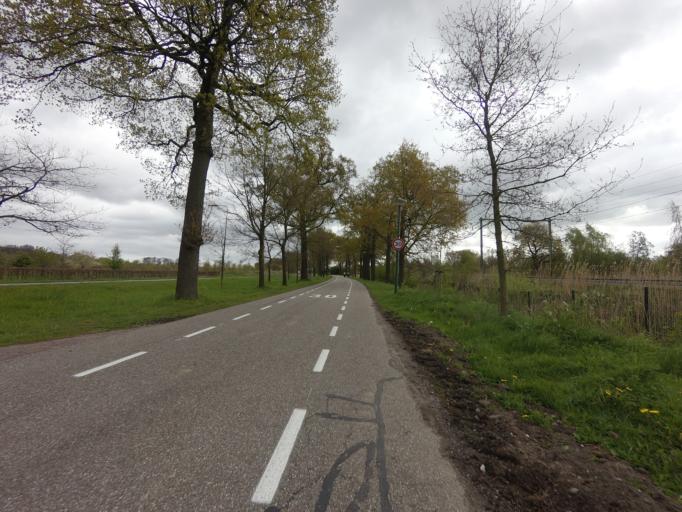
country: NL
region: Utrecht
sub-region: Gemeente Utrecht
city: Lunetten
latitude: 52.0651
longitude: 5.1590
